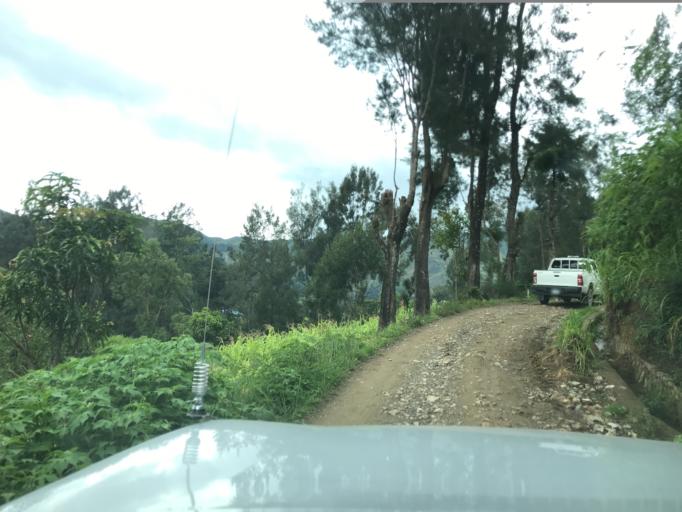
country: TL
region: Aileu
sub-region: Aileu Villa
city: Aileu
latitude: -8.8509
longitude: 125.5866
